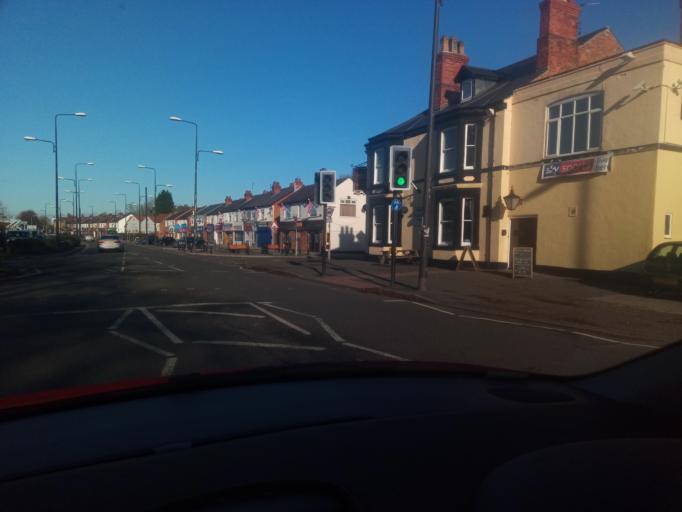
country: GB
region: England
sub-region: Derby
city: Derby
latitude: 52.8891
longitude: -1.4511
